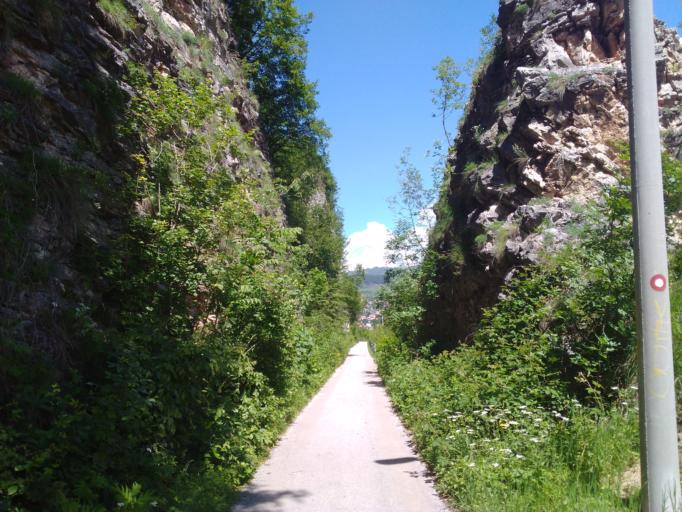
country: BA
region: Federation of Bosnia and Herzegovina
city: Kobilja Glava
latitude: 43.8515
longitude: 18.4569
